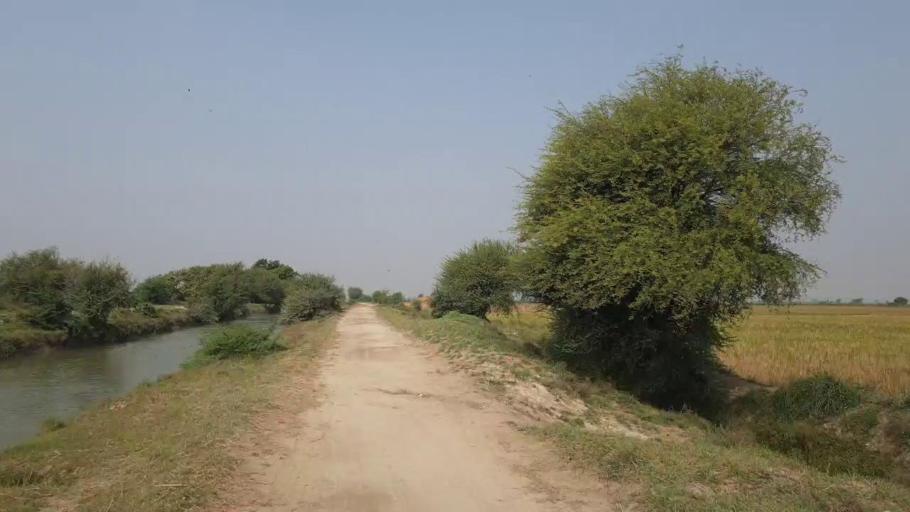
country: PK
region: Sindh
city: Kario
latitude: 24.8441
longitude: 68.5368
